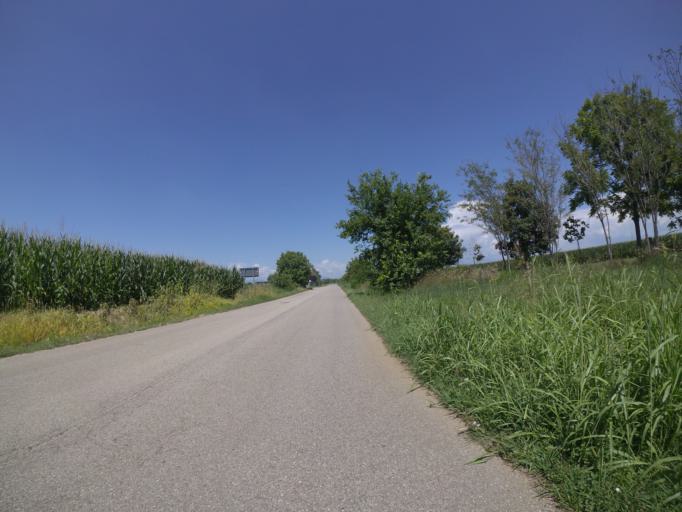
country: IT
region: Friuli Venezia Giulia
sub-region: Provincia di Udine
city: Talmassons
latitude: 45.9378
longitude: 13.1147
